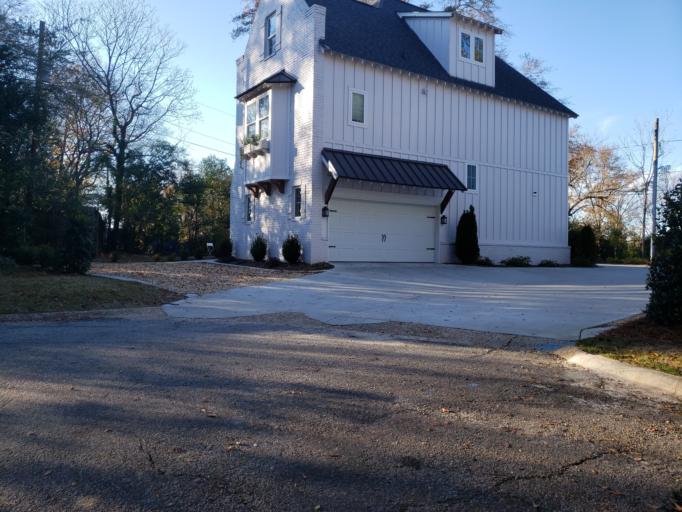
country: US
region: Alabama
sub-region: Lee County
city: Auburn
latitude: 32.5999
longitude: -85.4777
